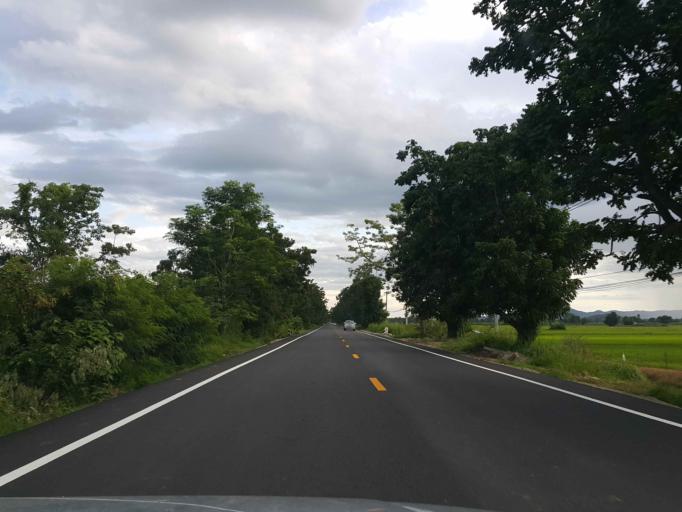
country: TH
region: Sukhothai
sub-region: Amphoe Si Satchanalai
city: Si Satchanalai
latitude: 17.4908
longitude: 99.7485
